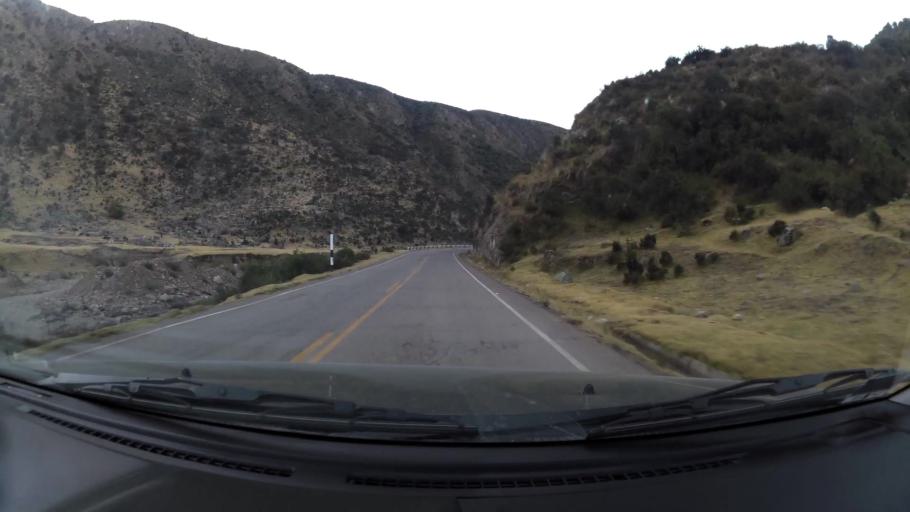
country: PE
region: Ayacucho
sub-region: Provincia de Huamanga
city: Vinchos
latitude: -13.3494
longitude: -74.3977
